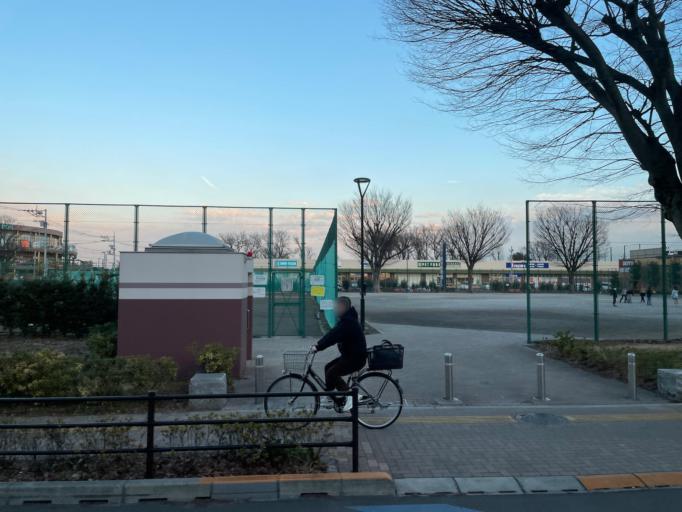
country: JP
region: Tokyo
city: Tanashicho
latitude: 35.7720
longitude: 139.5429
